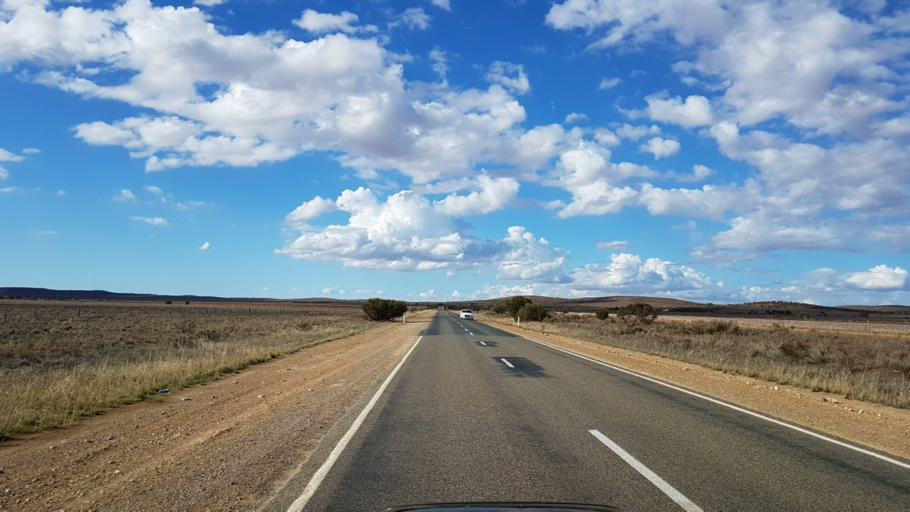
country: AU
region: South Australia
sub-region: Peterborough
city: Peterborough
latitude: -32.9675
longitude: 138.8718
